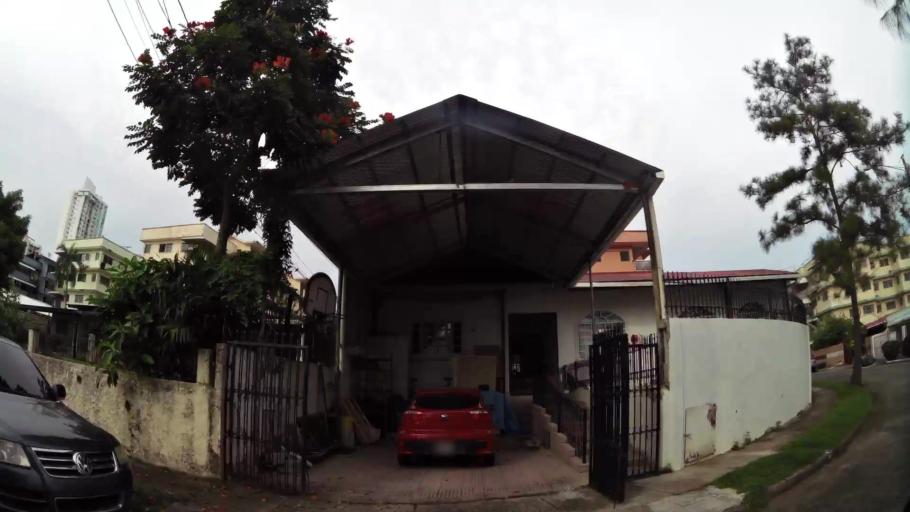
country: PA
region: Panama
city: Panama
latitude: 9.0073
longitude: -79.5109
